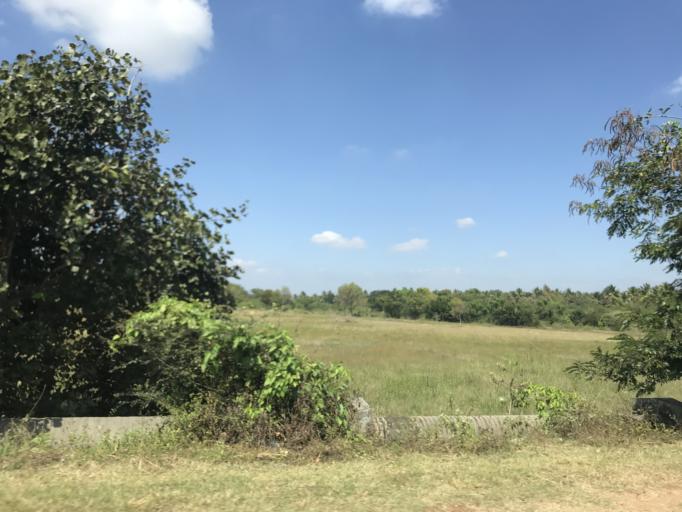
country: IN
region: Karnataka
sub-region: Mysore
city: Hunsur
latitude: 12.3602
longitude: 76.3012
